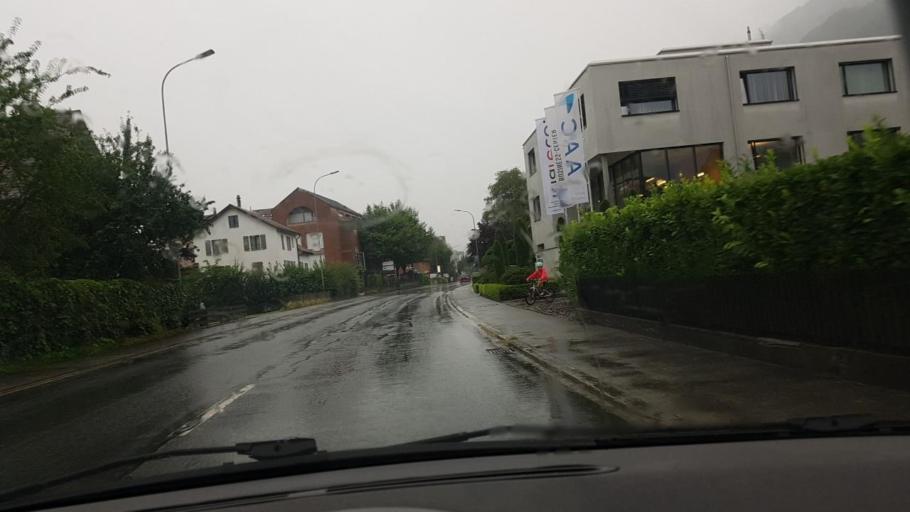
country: LI
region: Triesen
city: Triesen
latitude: 47.1138
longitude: 9.5237
